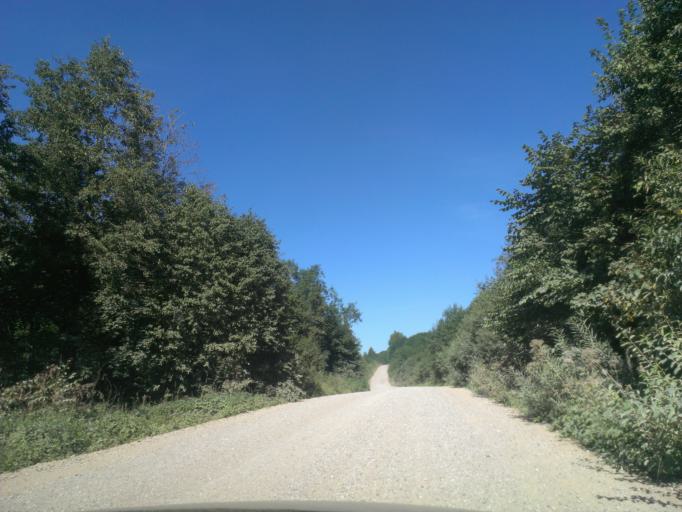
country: LV
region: Amatas Novads
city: Drabesi
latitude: 57.0608
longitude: 25.1727
